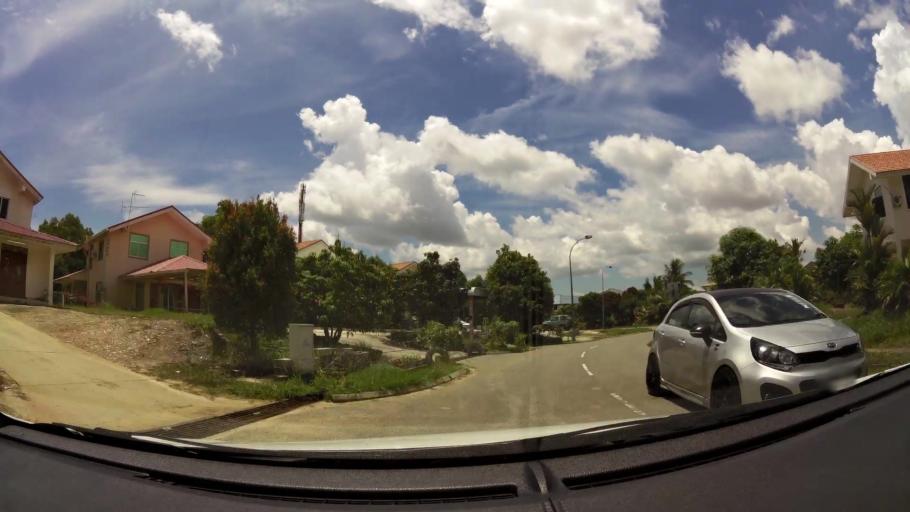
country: BN
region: Brunei and Muara
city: Bandar Seri Begawan
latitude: 4.9647
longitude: 114.9111
